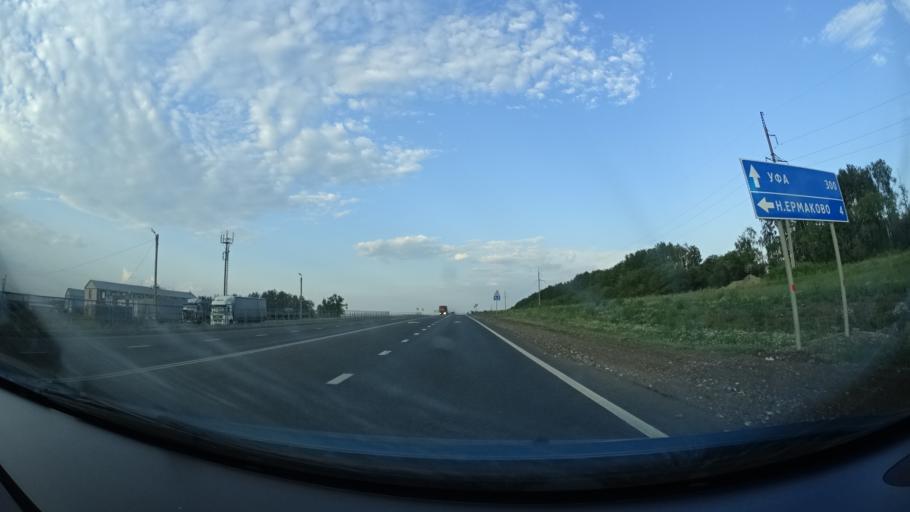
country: RU
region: Samara
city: Kamyshla
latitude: 54.0277
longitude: 51.8944
